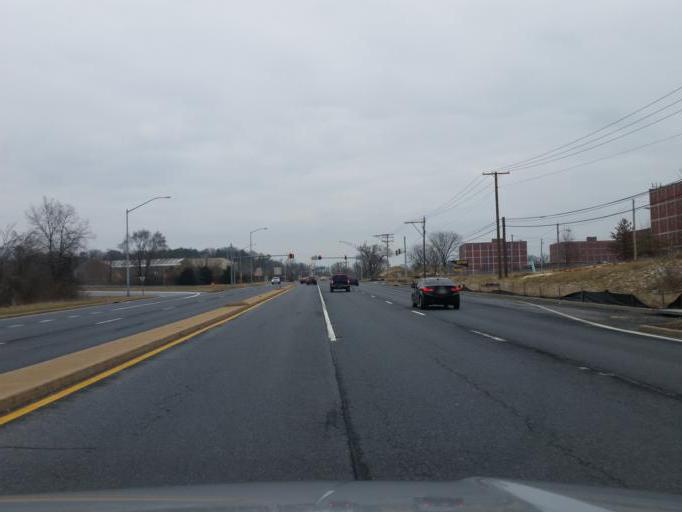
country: US
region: Maryland
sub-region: Howard County
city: Elkridge
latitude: 39.2215
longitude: -76.7013
